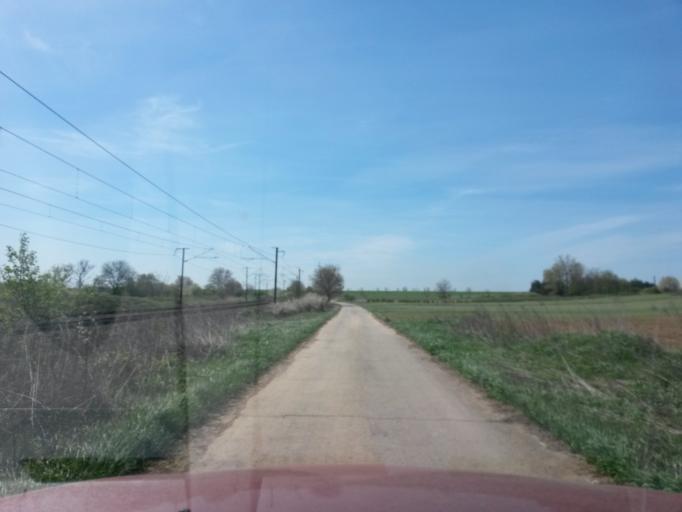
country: SK
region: Kosicky
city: Kosice
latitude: 48.6563
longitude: 21.2612
